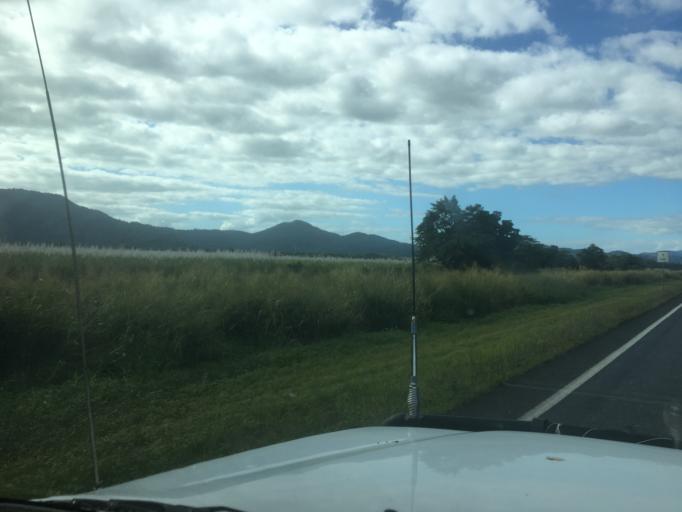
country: AU
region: Queensland
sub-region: Cassowary Coast
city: Innisfail
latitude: -17.2881
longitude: 145.9234
